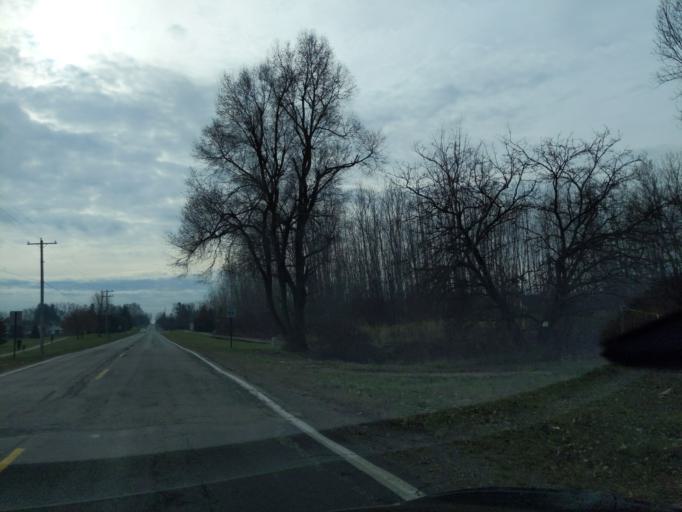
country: US
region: Michigan
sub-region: Ingham County
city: Holt
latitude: 42.6255
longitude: -84.5232
